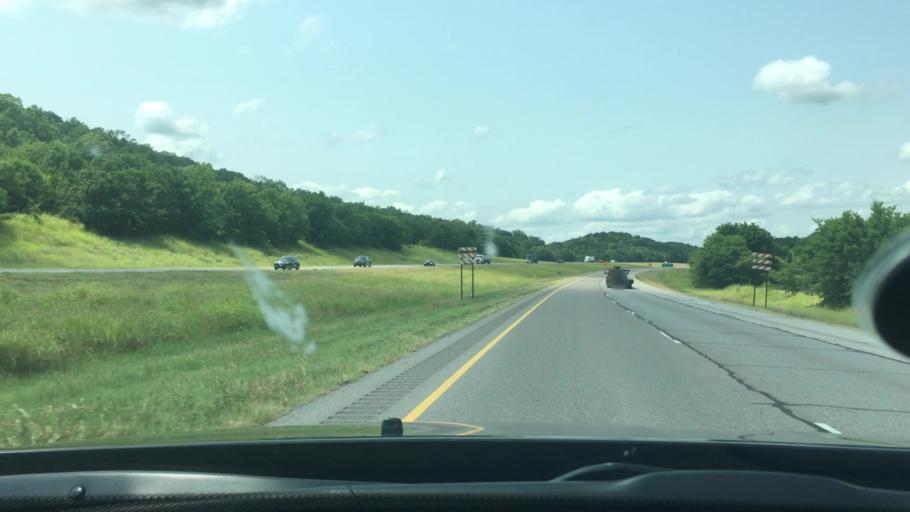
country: US
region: Oklahoma
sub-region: Murray County
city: Davis
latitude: 34.4665
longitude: -97.1503
